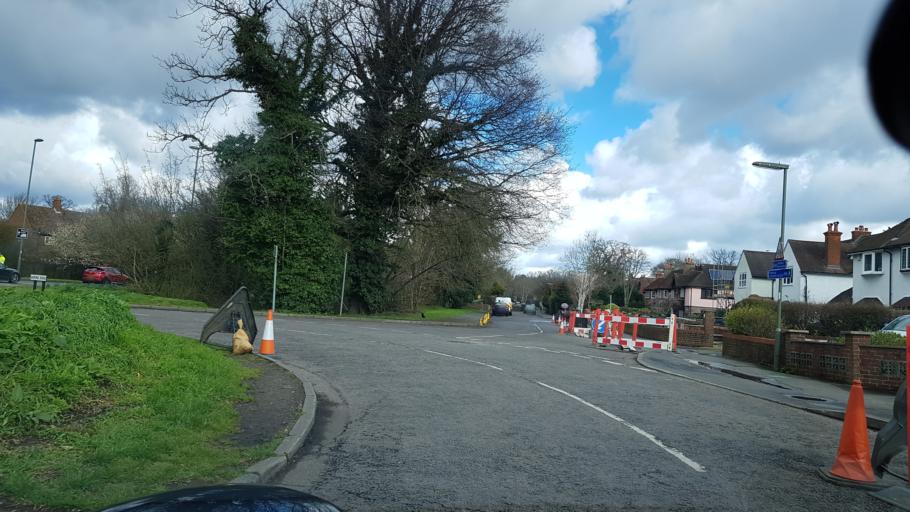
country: GB
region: England
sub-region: Surrey
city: Guildford
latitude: 51.2595
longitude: -0.5730
